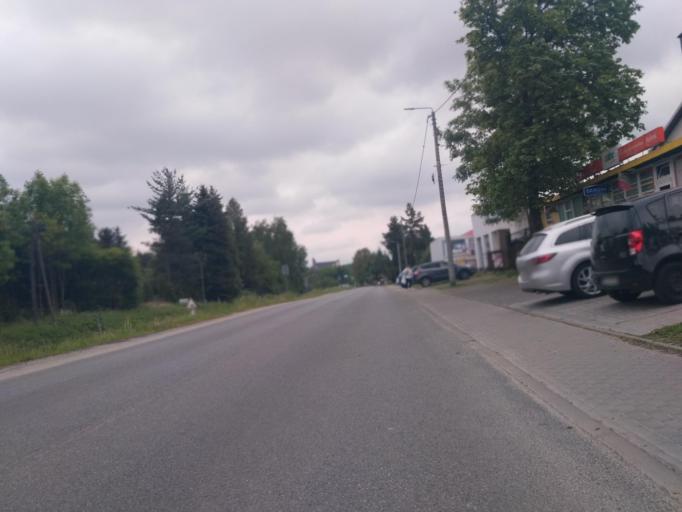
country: PL
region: Subcarpathian Voivodeship
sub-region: Krosno
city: Krosno
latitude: 49.6893
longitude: 21.7590
